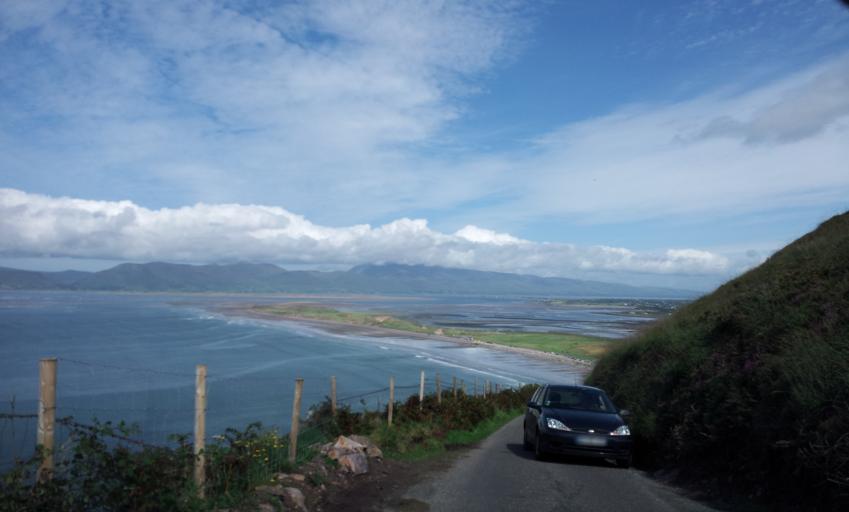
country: IE
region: Munster
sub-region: Ciarrai
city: Killorglin
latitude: 52.0481
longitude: -9.9871
